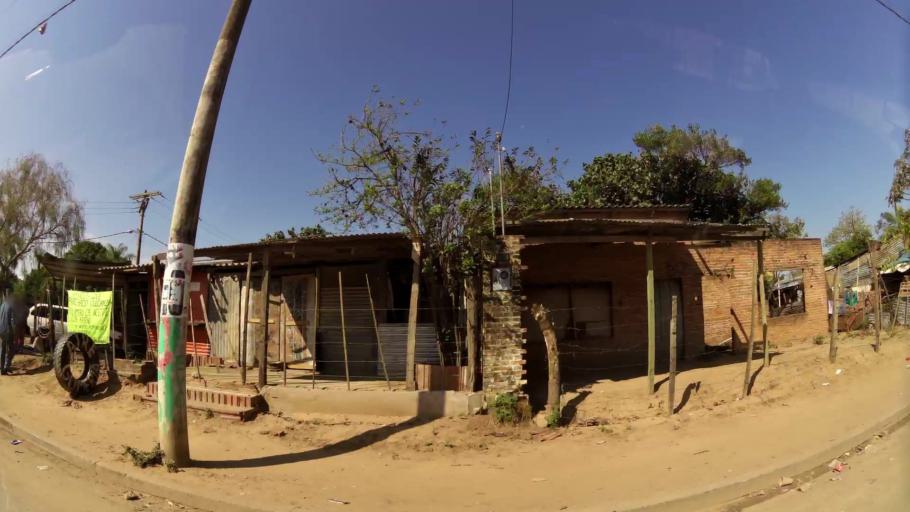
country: BO
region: Santa Cruz
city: Cotoca
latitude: -17.7385
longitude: -63.0741
